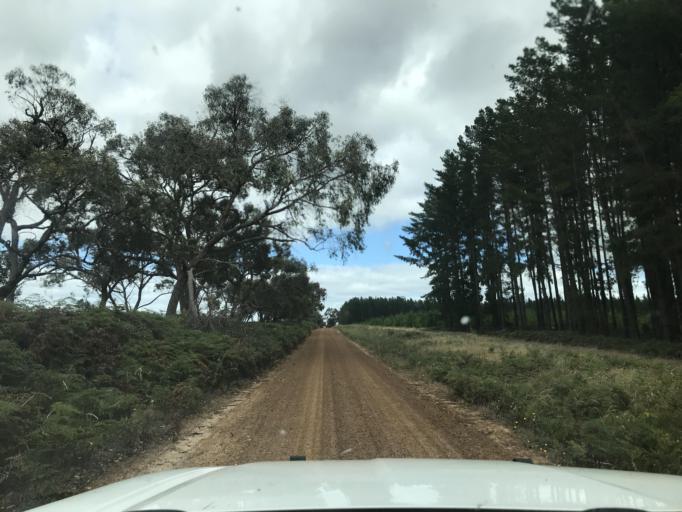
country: AU
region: South Australia
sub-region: Wattle Range
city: Penola
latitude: -37.3174
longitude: 141.1547
